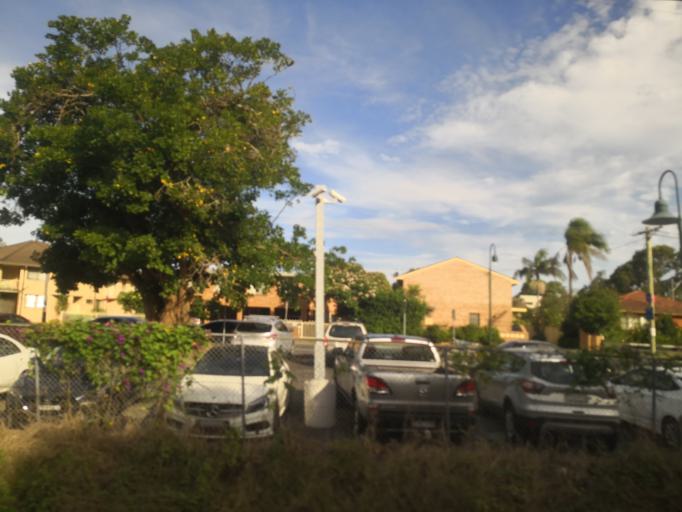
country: AU
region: New South Wales
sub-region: Gosford Shire
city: Blackwall
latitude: -33.4885
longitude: 151.3200
